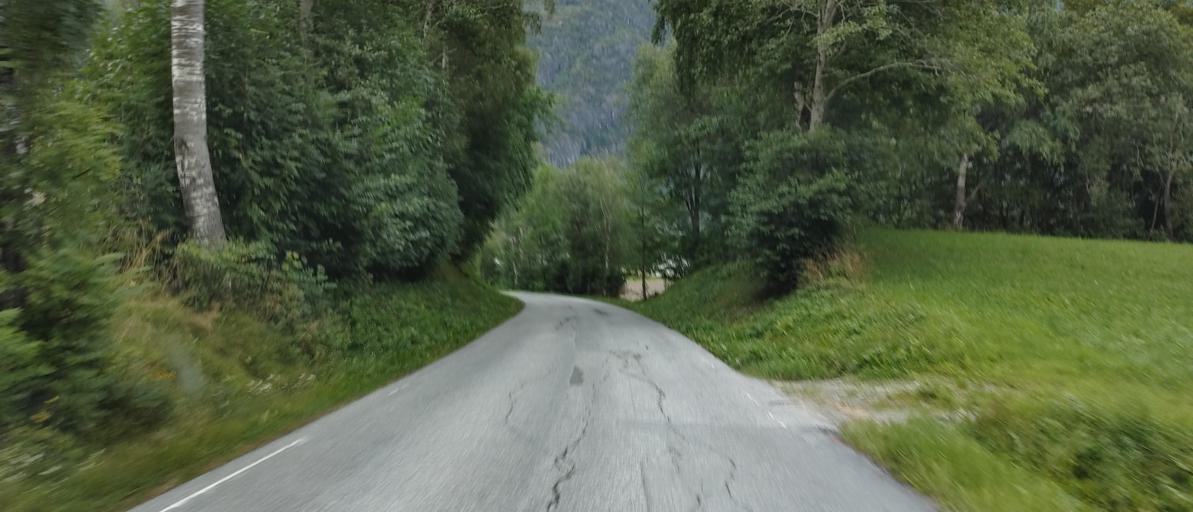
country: NO
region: More og Romsdal
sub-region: Rauma
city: Andalsnes
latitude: 62.5270
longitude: 7.7200
